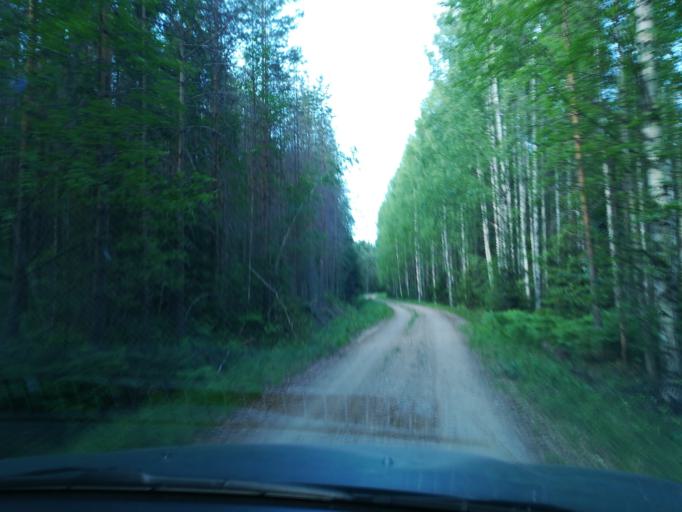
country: FI
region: South Karelia
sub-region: Imatra
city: Ruokolahti
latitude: 61.5456
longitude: 28.8098
